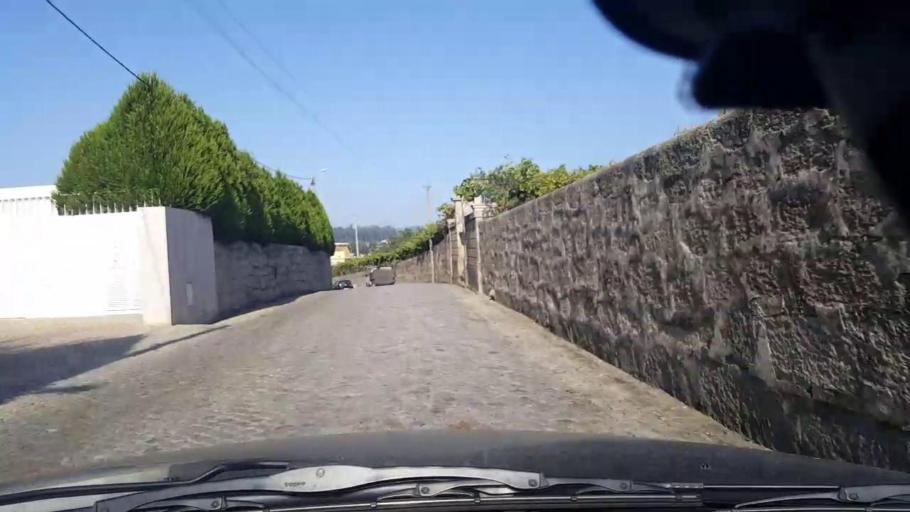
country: PT
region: Porto
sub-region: Maia
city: Gemunde
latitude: 41.2758
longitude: -8.6724
